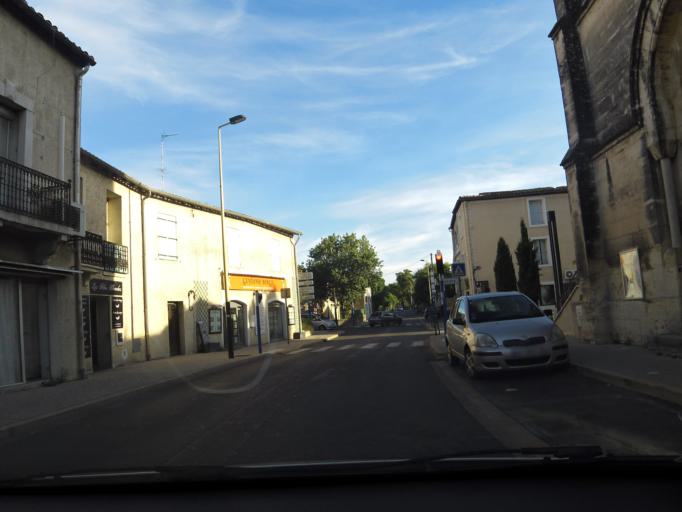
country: FR
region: Languedoc-Roussillon
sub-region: Departement de l'Herault
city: Prades-le-Lez
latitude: 43.6978
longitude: 3.8630
